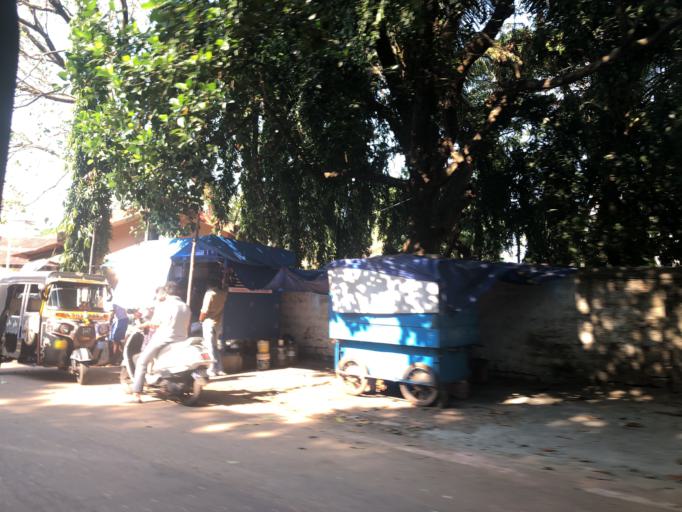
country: IN
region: Karnataka
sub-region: Dakshina Kannada
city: Mangalore
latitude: 12.8886
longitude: 74.8306
